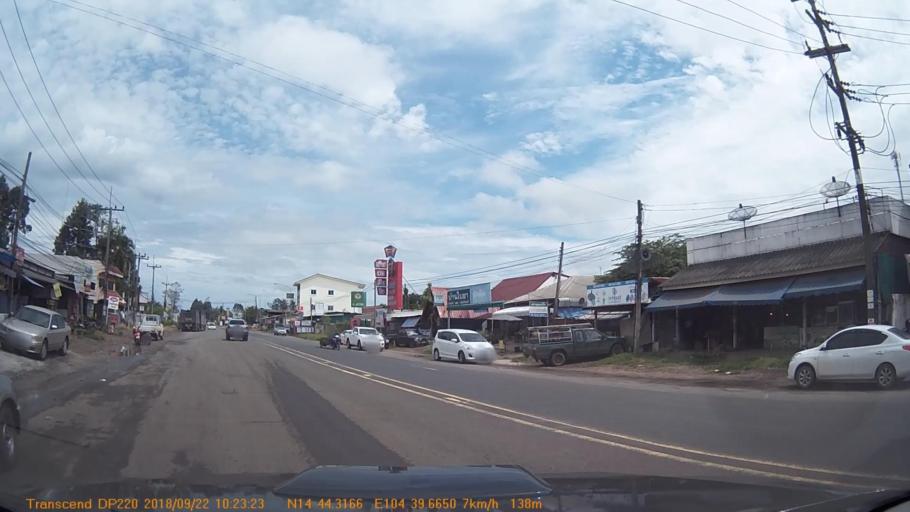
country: TH
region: Sisaket
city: Benchalak
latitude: 14.7385
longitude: 104.6611
